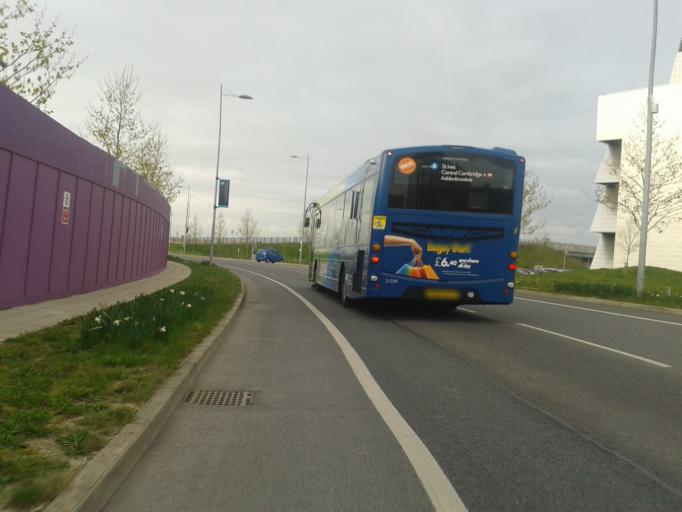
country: GB
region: England
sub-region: Cambridgeshire
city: Cambridge
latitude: 52.1755
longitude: 0.1345
